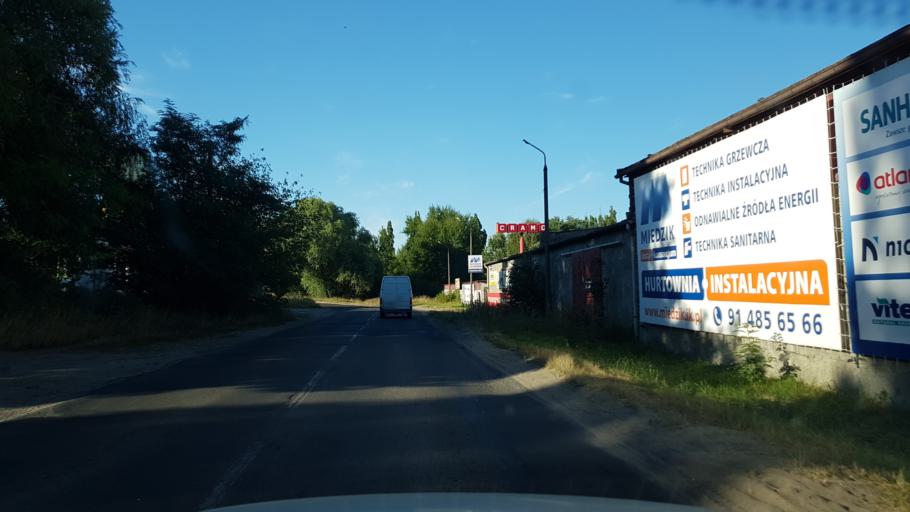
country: PL
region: West Pomeranian Voivodeship
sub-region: Szczecin
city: Szczecin
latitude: 53.3978
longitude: 14.5319
